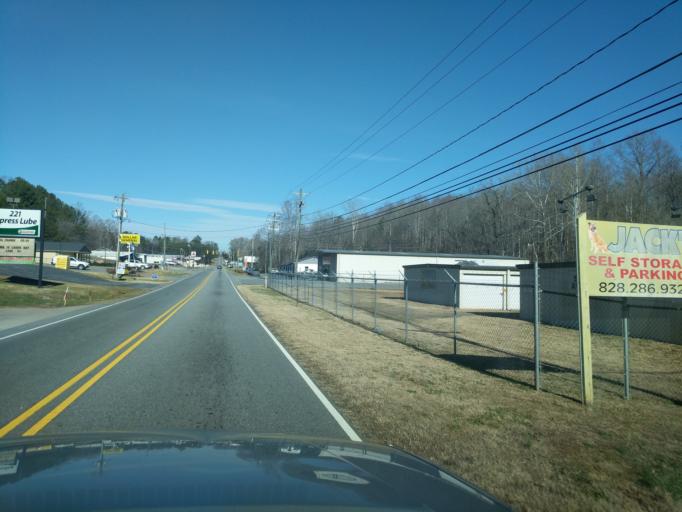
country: US
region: North Carolina
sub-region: Rutherford County
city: Rutherfordton
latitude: 35.3520
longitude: -81.9615
